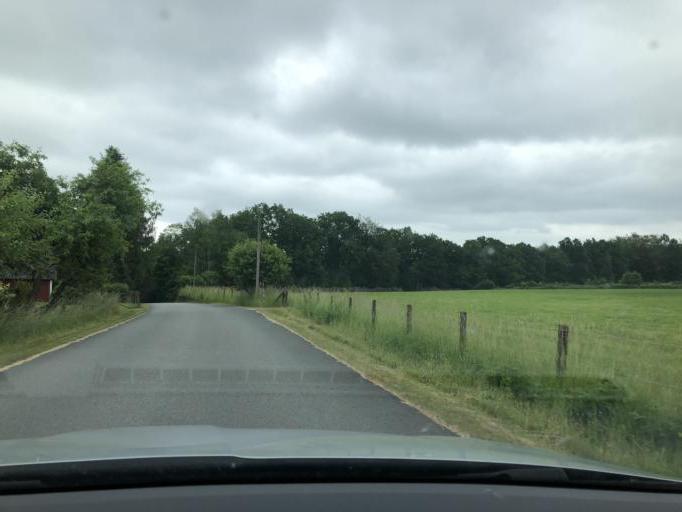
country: SE
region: Blekinge
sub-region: Solvesborgs Kommun
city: Soelvesborg
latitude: 56.1428
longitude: 14.6015
